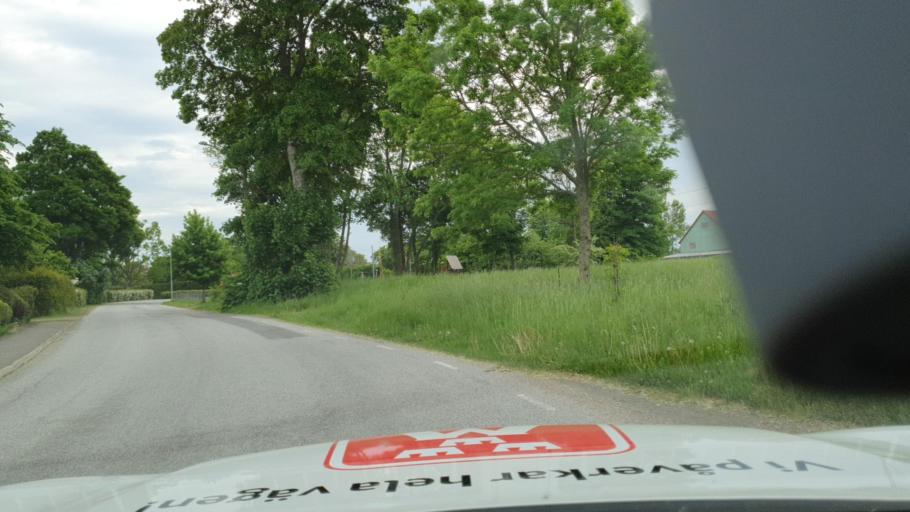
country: SE
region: Skane
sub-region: Ystads Kommun
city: Kopingebro
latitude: 55.4822
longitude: 13.9466
